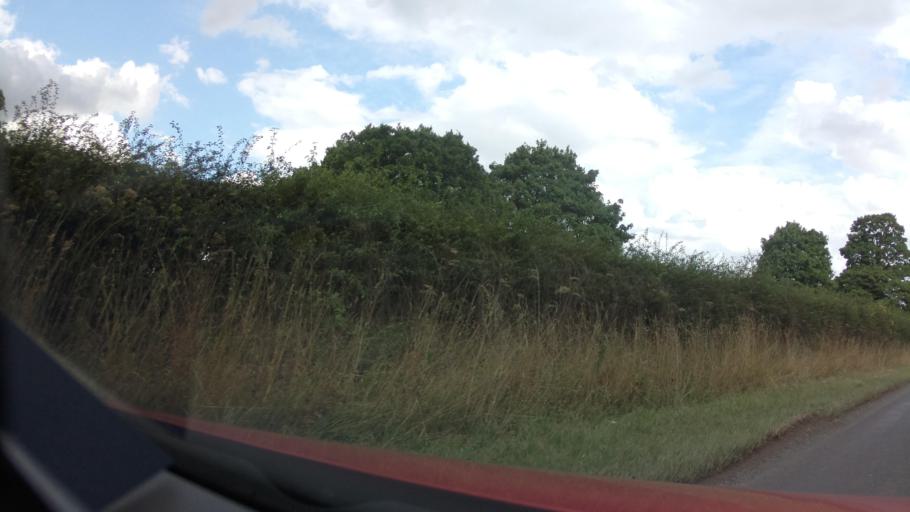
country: GB
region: England
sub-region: North Yorkshire
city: Ripon
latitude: 54.1533
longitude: -1.5344
